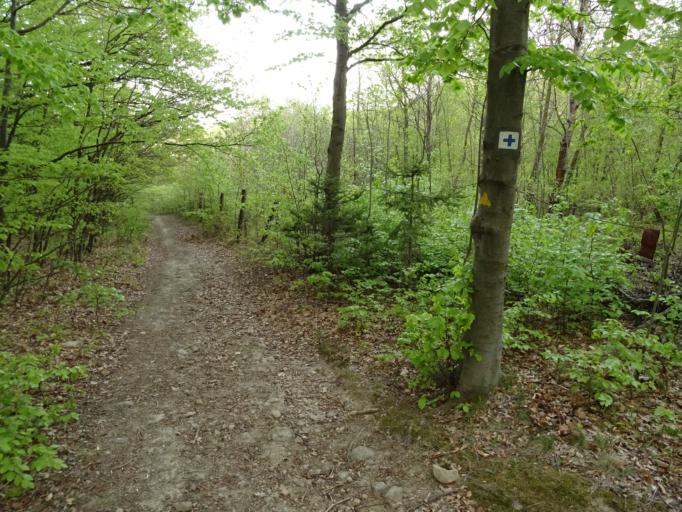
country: HU
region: Borsod-Abauj-Zemplen
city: Gonc
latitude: 48.5423
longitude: 21.4783
